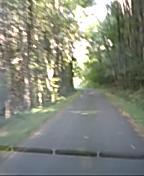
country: FR
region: Rhone-Alpes
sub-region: Departement de la Loire
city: La Pacaudiere
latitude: 46.1321
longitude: 3.7890
